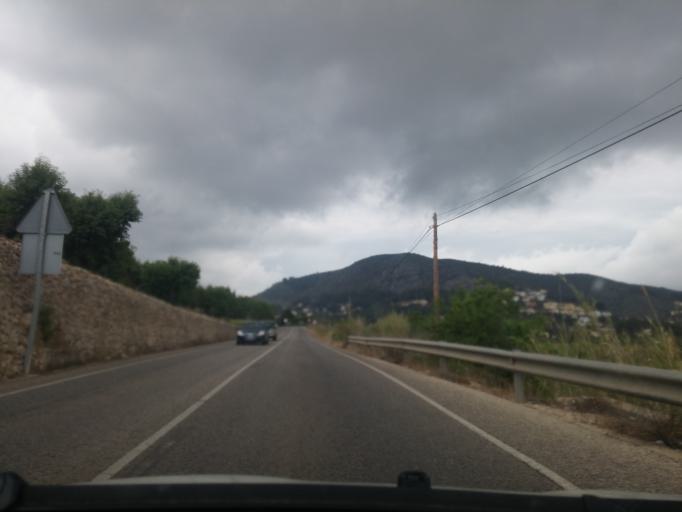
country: ES
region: Valencia
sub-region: Provincia de Alicante
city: Alcalali
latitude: 38.7485
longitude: -0.0345
